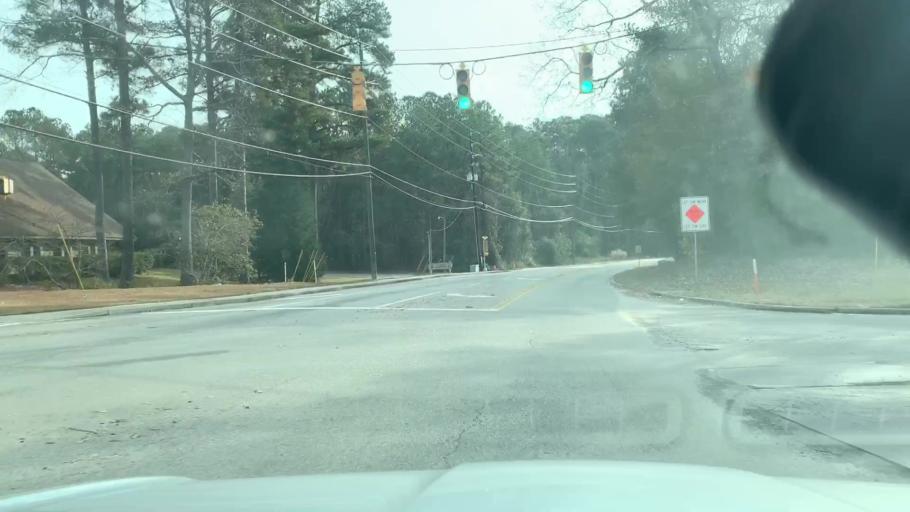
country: US
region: South Carolina
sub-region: Richland County
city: Woodfield
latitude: 34.0818
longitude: -80.9244
